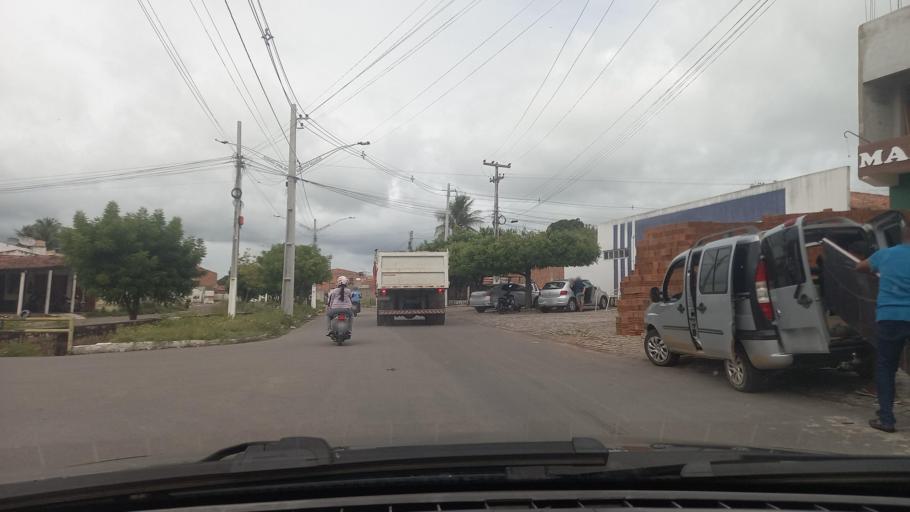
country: BR
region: Alagoas
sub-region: Delmiro Gouveia
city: Delmiro Gouveia
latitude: -9.3830
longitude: -38.0036
